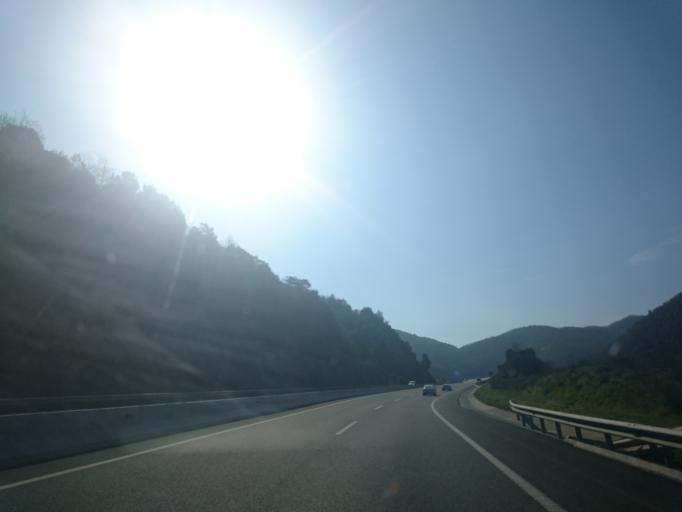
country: ES
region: Catalonia
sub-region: Provincia de Girona
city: Viladrau
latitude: 41.8904
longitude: 2.3826
